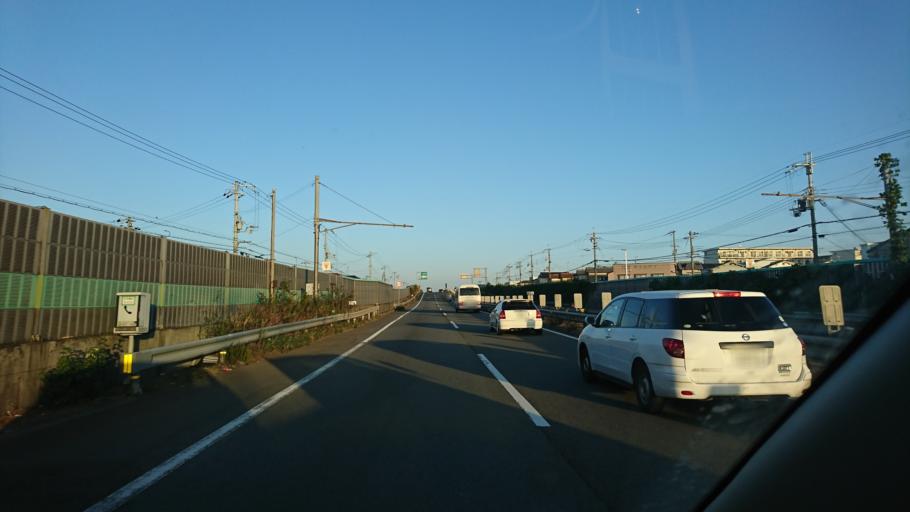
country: JP
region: Hyogo
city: Kakogawacho-honmachi
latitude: 34.7285
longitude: 134.8900
